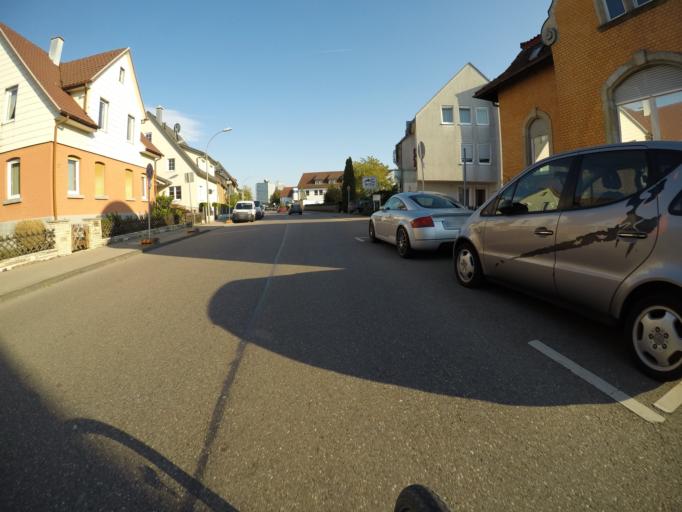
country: DE
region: Baden-Wuerttemberg
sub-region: Regierungsbezirk Stuttgart
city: Leinfelden-Echterdingen
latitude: 48.7245
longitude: 9.1543
